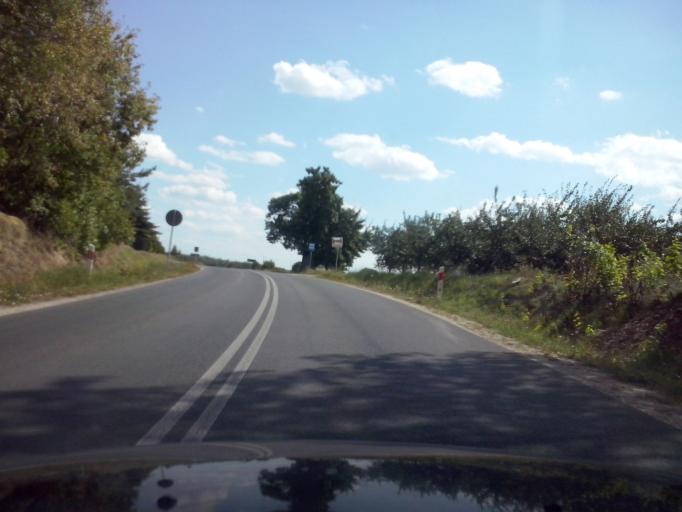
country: PL
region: Swietokrzyskie
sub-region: Powiat staszowski
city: Szydlow
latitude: 50.5867
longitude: 20.9642
